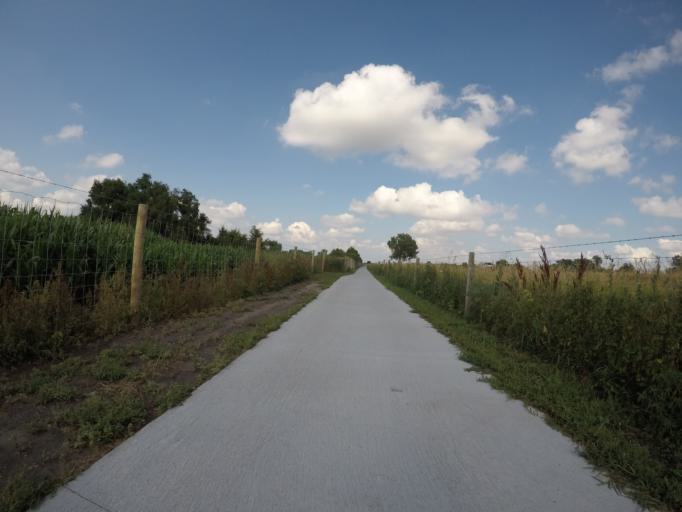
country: US
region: Nebraska
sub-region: Buffalo County
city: Kearney
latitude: 40.6775
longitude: -98.9993
